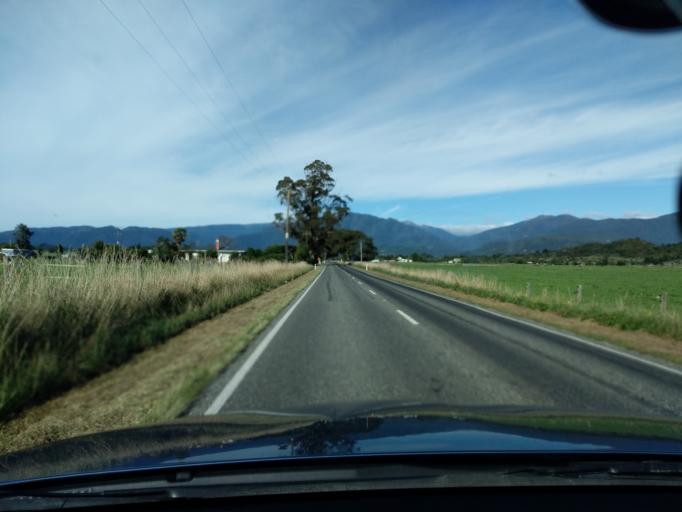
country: NZ
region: Tasman
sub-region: Tasman District
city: Takaka
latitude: -40.8479
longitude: 172.8353
